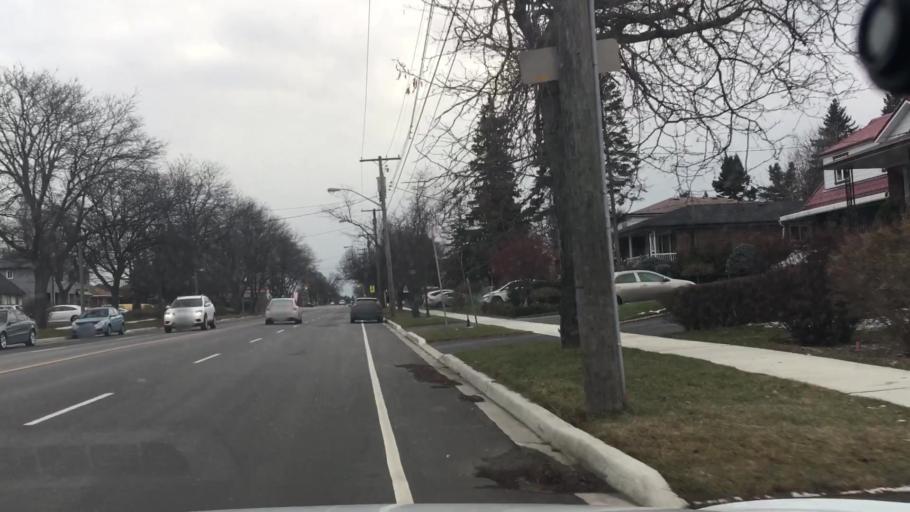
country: CA
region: Ontario
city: Scarborough
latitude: 43.7485
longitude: -79.2320
